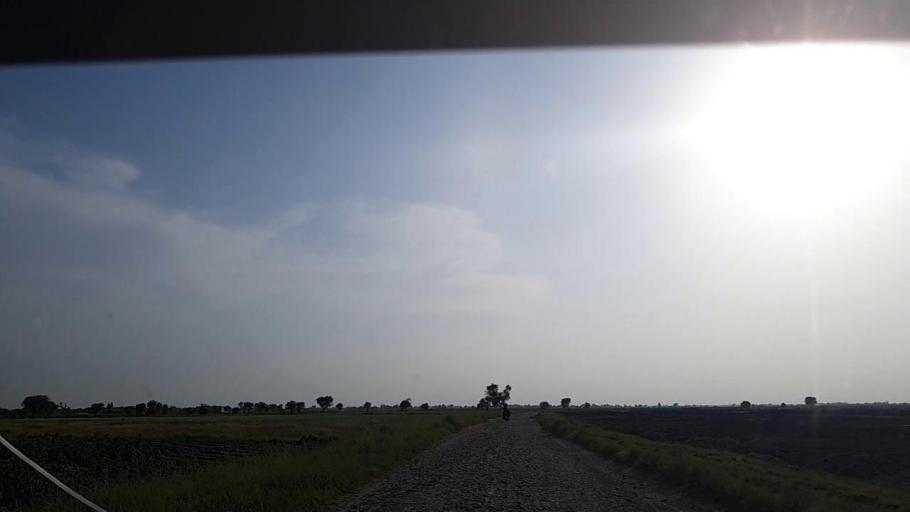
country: PK
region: Sindh
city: Khanpur
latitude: 27.8335
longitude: 69.3656
